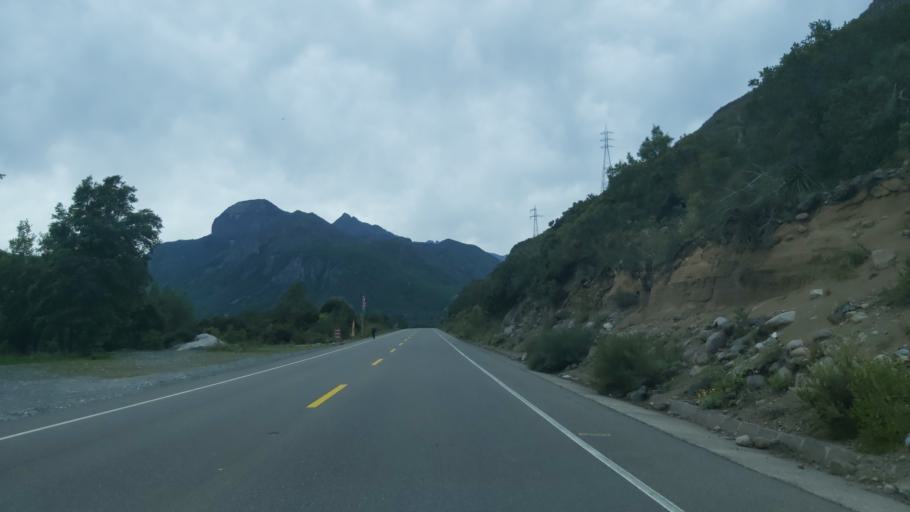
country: CL
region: Maule
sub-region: Provincia de Linares
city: Colbun
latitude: -35.7089
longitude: -71.0874
